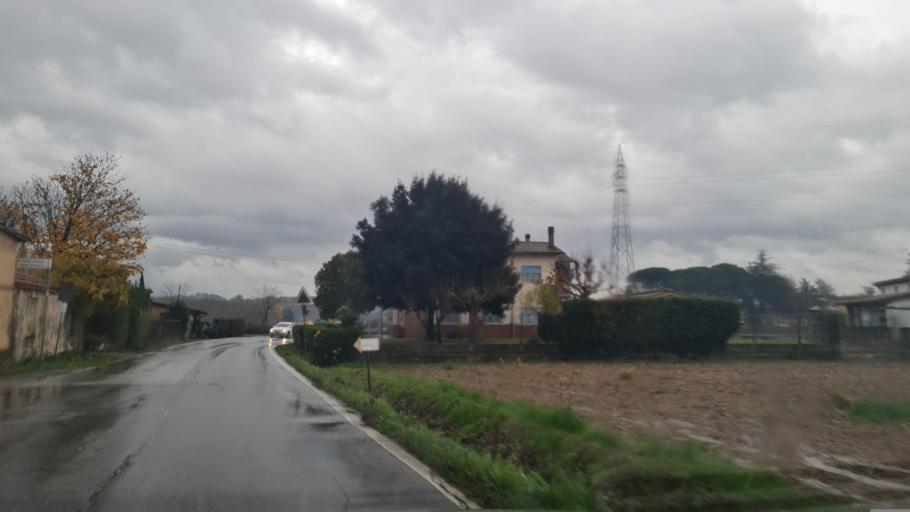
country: IT
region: Tuscany
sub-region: Provincia di Lucca
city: Lucca
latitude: 43.8627
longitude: 10.4787
